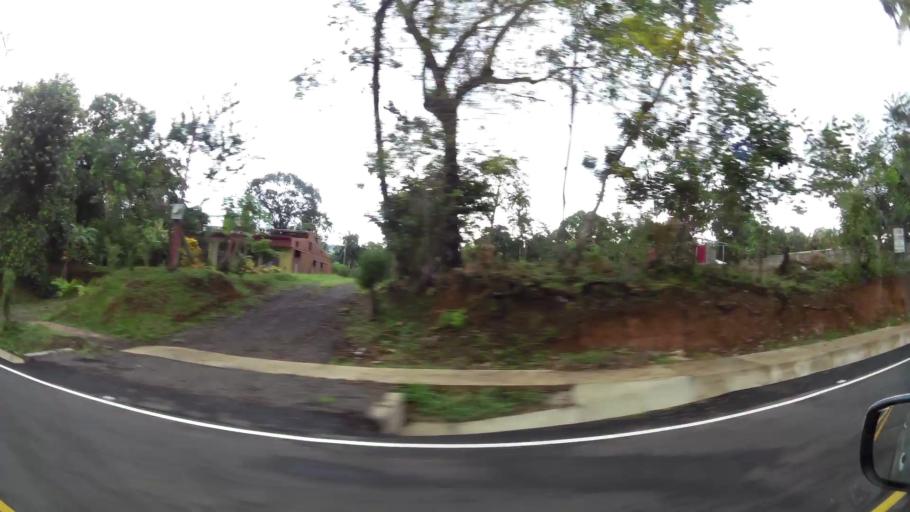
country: CR
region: Alajuela
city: Orotina
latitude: 9.9452
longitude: -84.5498
